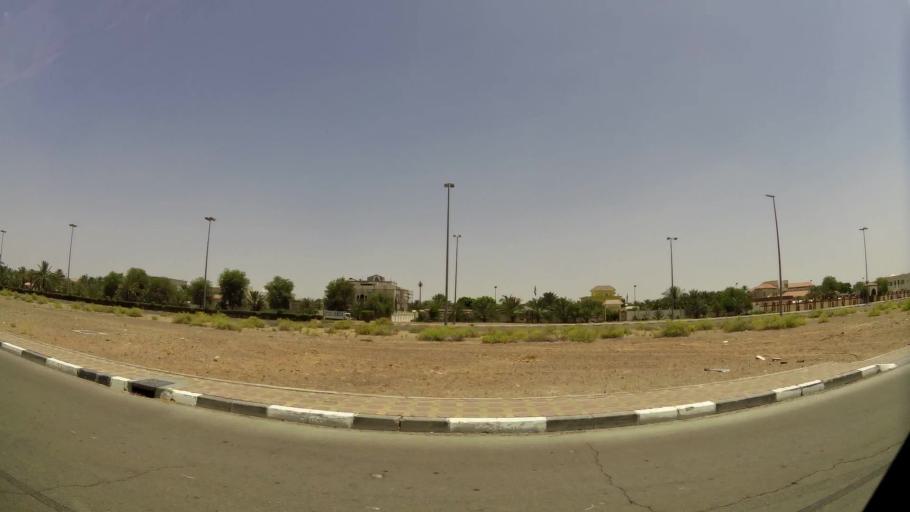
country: OM
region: Al Buraimi
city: Al Buraymi
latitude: 24.2597
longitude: 55.7143
